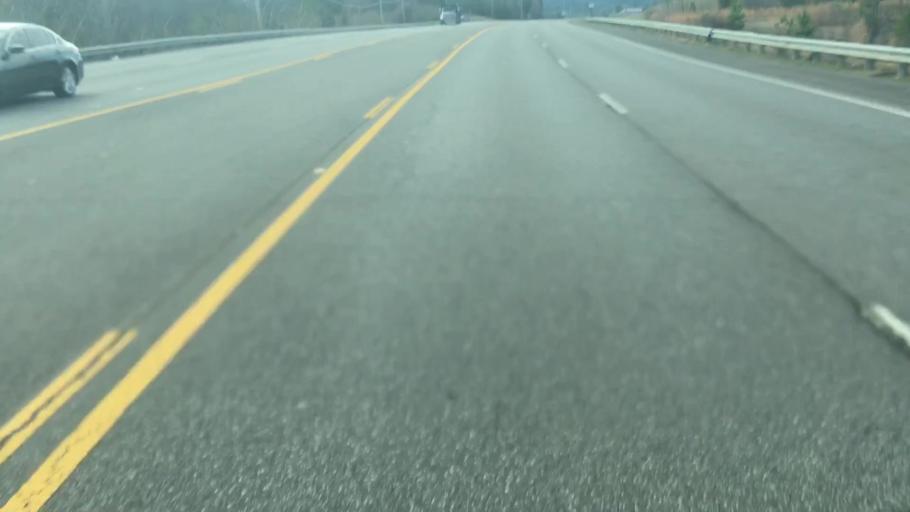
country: US
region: Alabama
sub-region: Walker County
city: Jasper
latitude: 33.8016
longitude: -87.2361
